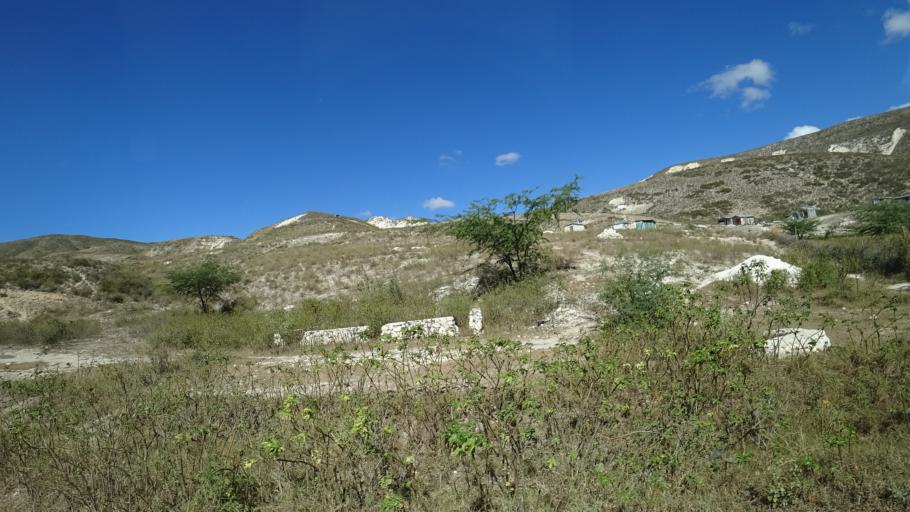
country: HT
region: Ouest
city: Croix des Bouquets
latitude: 18.6757
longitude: -72.2579
